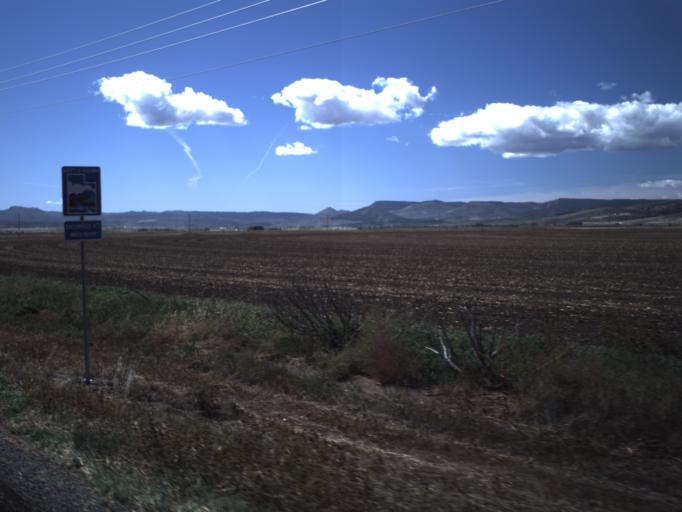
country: US
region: Utah
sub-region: Washington County
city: Enterprise
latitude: 37.6380
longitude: -113.6612
